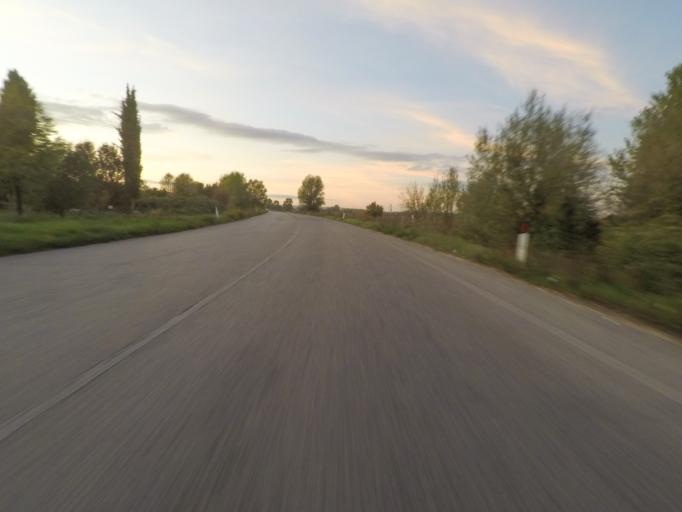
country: IT
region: Tuscany
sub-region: Provincia di Siena
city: Sinalunga
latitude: 43.2146
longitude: 11.7618
